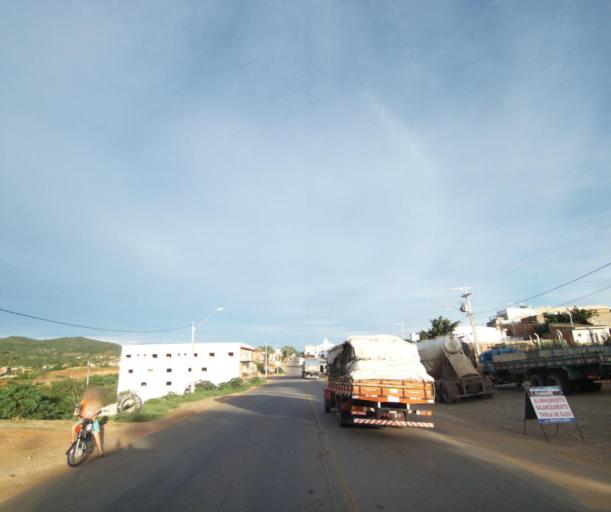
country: BR
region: Bahia
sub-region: Cacule
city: Cacule
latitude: -14.2050
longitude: -42.1180
